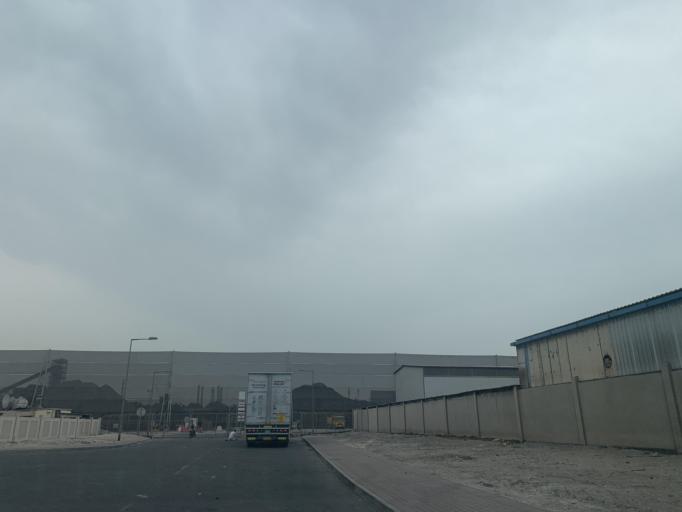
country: BH
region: Muharraq
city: Al Hadd
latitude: 26.2028
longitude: 50.6836
